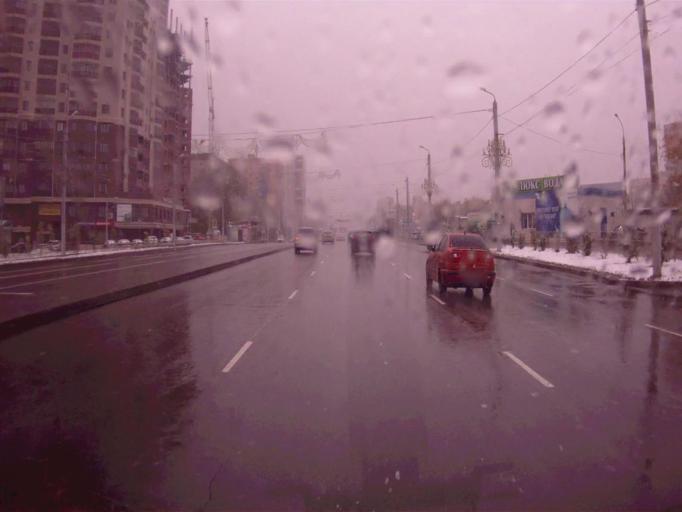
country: RU
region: Chelyabinsk
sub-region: Gorod Chelyabinsk
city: Chelyabinsk
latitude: 55.1453
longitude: 61.4014
